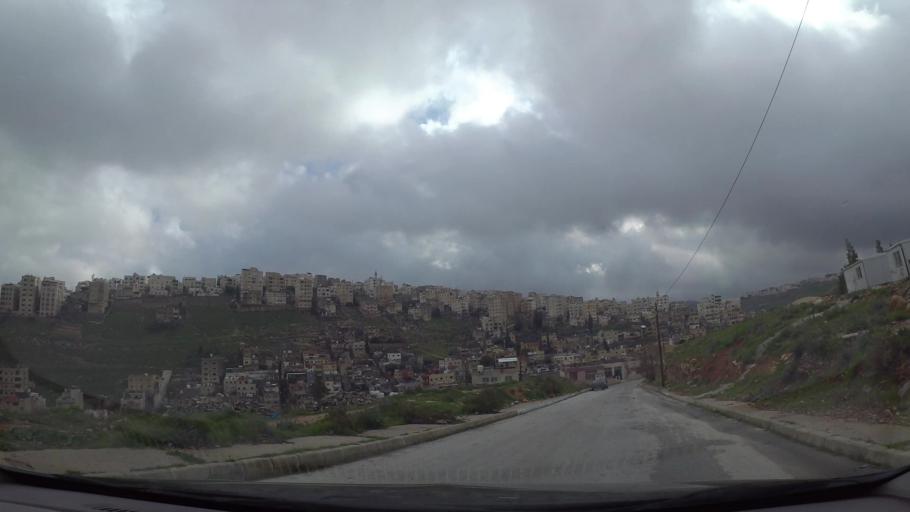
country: JO
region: Amman
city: Amman
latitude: 31.9401
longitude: 35.9056
